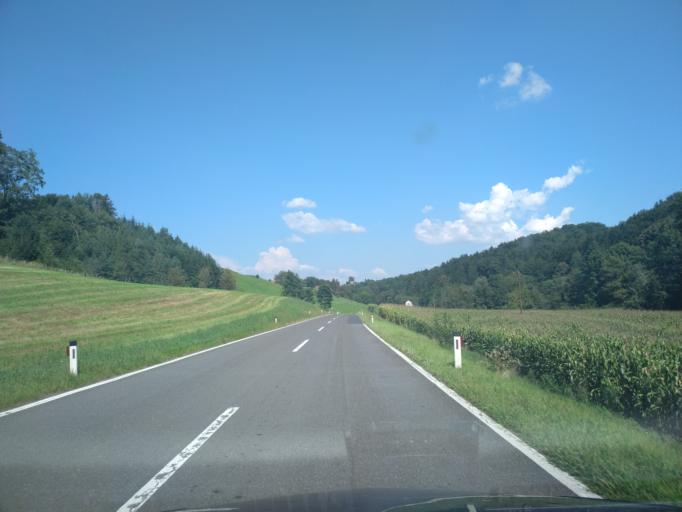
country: AT
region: Styria
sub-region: Politischer Bezirk Leibnitz
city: Leutschach
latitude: 46.6984
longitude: 15.4961
